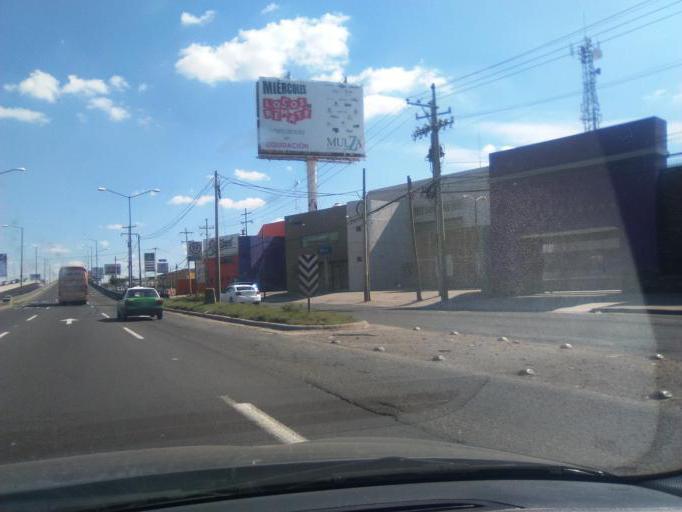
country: MX
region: Guanajuato
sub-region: Leon
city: Fraccionamiento Paraiso Real
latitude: 21.0925
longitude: -101.6236
